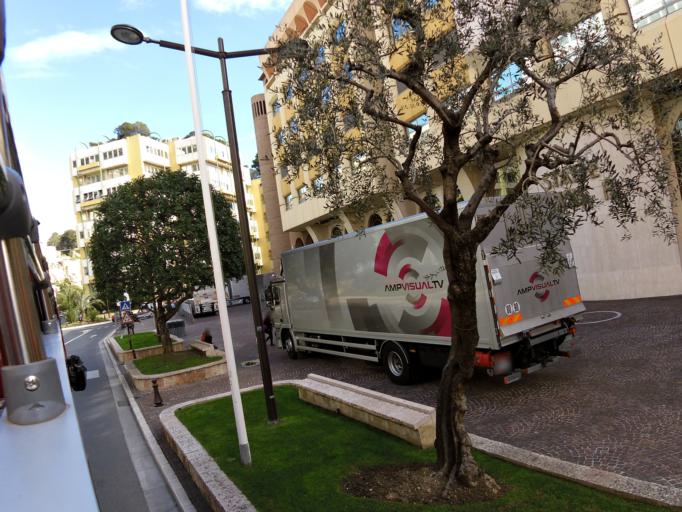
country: MC
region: Commune de Monaco
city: Fontvieille
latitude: 43.7282
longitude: 7.4144
